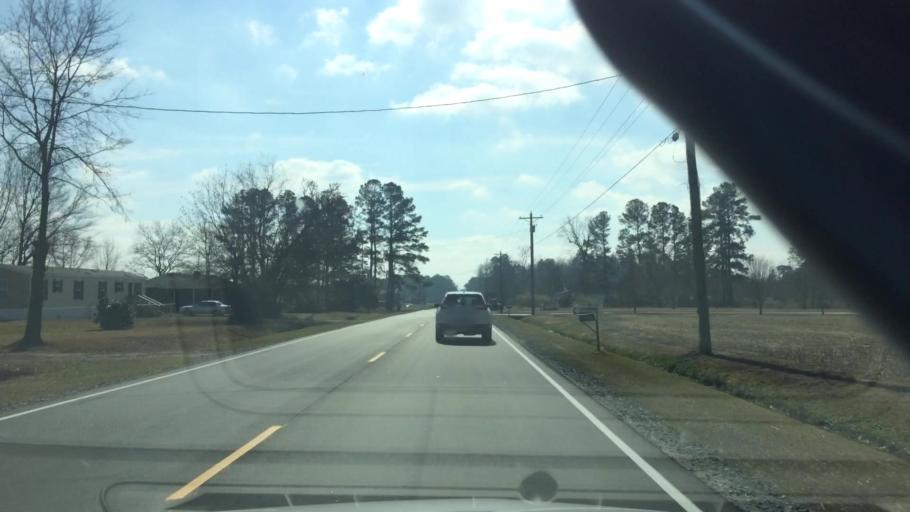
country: US
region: North Carolina
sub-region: Duplin County
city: Beulaville
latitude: 34.9721
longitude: -77.7619
